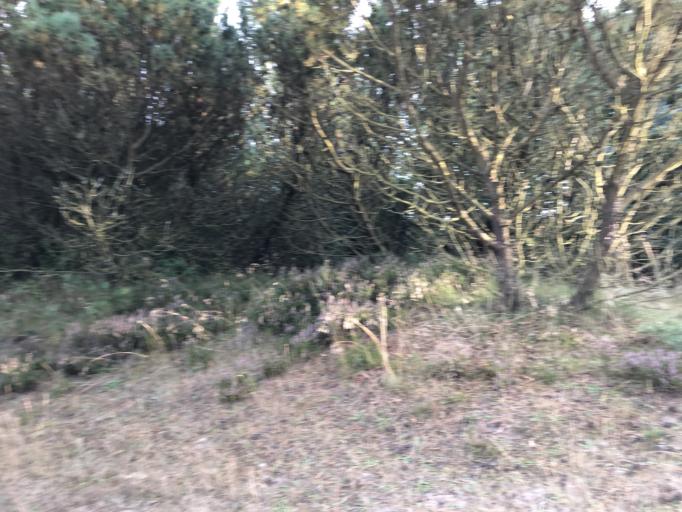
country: DK
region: Central Jutland
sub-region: Holstebro Kommune
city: Ulfborg
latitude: 56.2462
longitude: 8.4509
